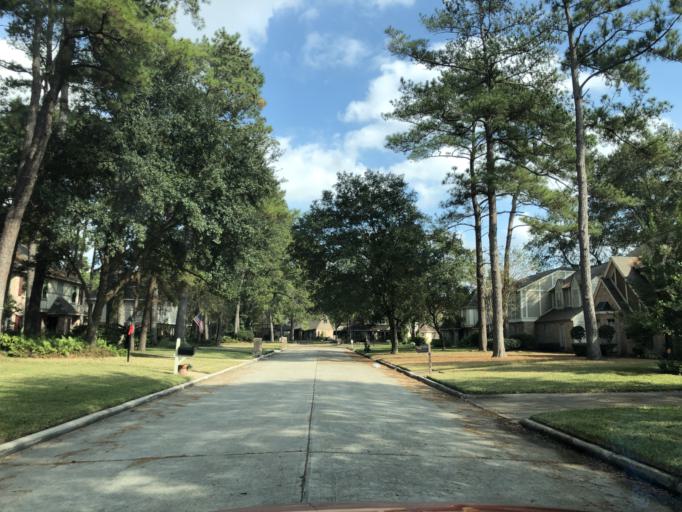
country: US
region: Texas
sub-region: Harris County
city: Tomball
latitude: 30.0238
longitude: -95.5485
